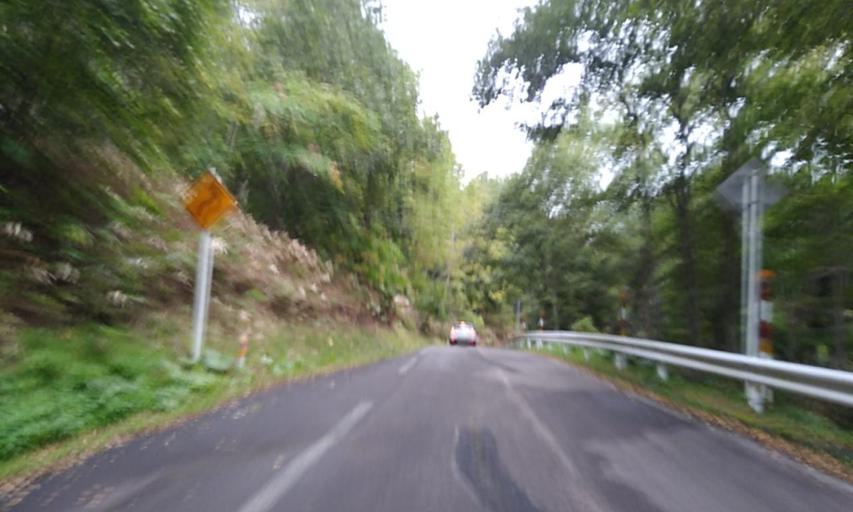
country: JP
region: Hokkaido
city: Bihoro
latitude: 43.5716
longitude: 144.1999
